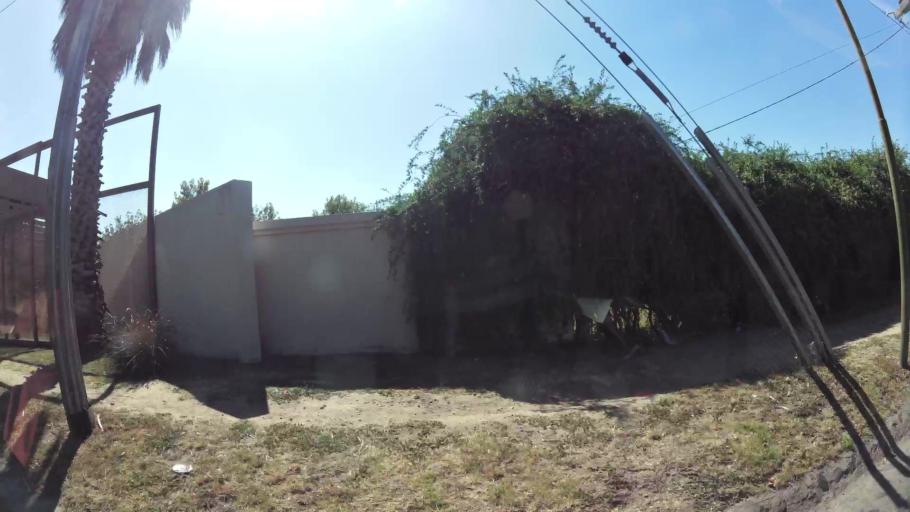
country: AR
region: Cordoba
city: Villa Allende
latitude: -31.2945
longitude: -64.2810
